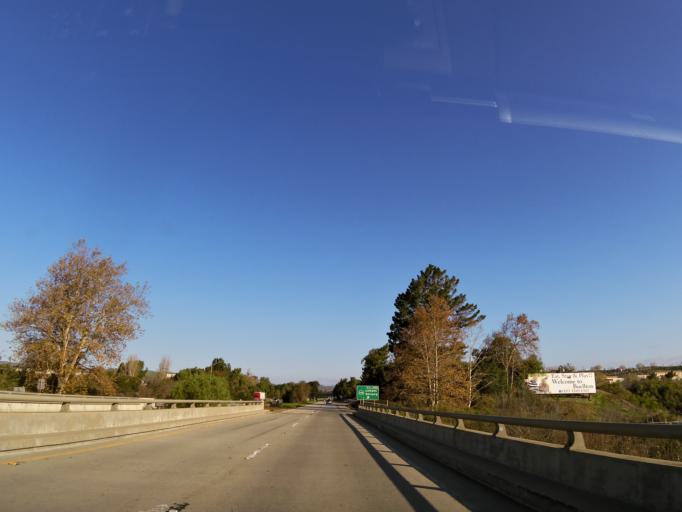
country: US
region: California
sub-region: Santa Barbara County
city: Buellton
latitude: 34.6075
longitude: -120.1909
